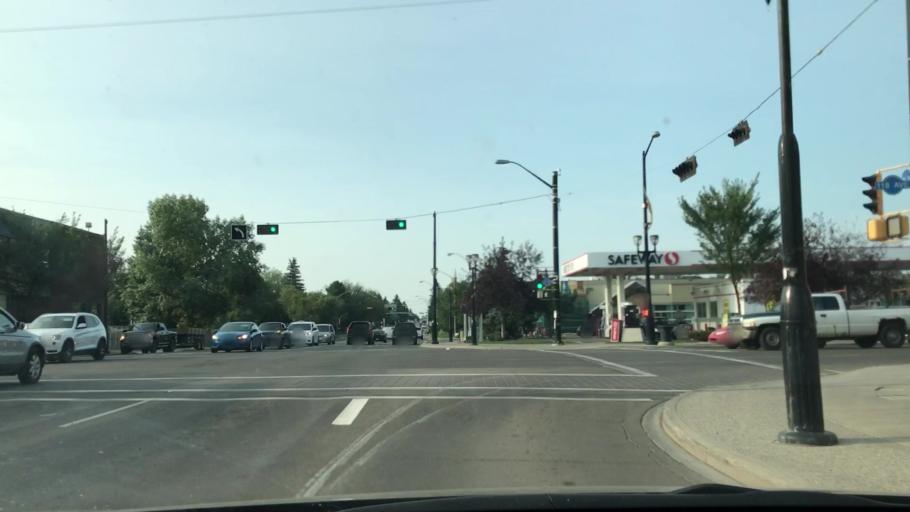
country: CA
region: Alberta
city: Edmonton
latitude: 53.5701
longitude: -113.4671
